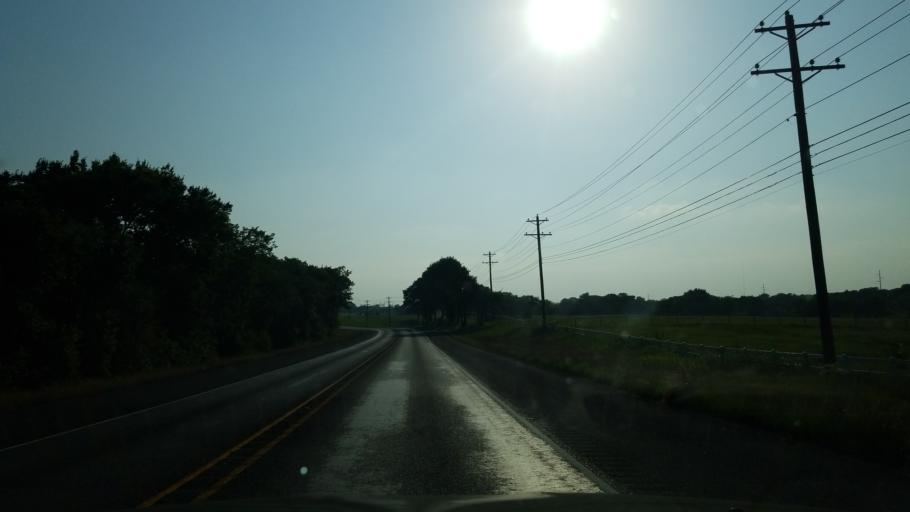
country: US
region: Texas
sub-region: Denton County
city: Aubrey
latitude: 33.3047
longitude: -97.0075
